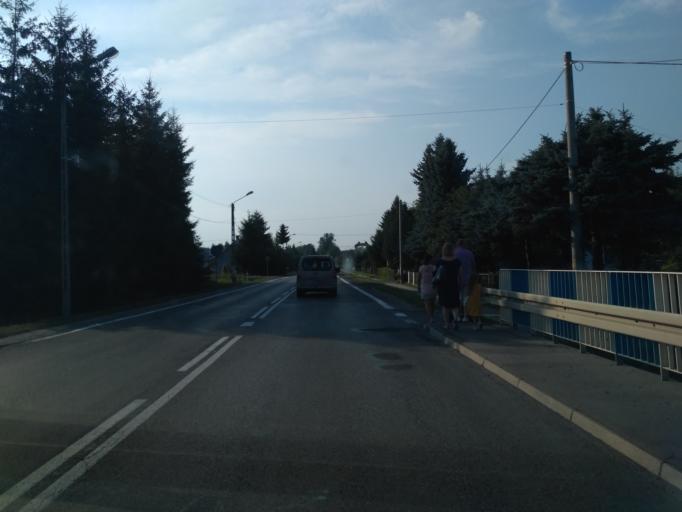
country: PL
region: Subcarpathian Voivodeship
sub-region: Powiat brzozowski
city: Grabownica Starzenska
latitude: 49.6598
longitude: 22.0759
